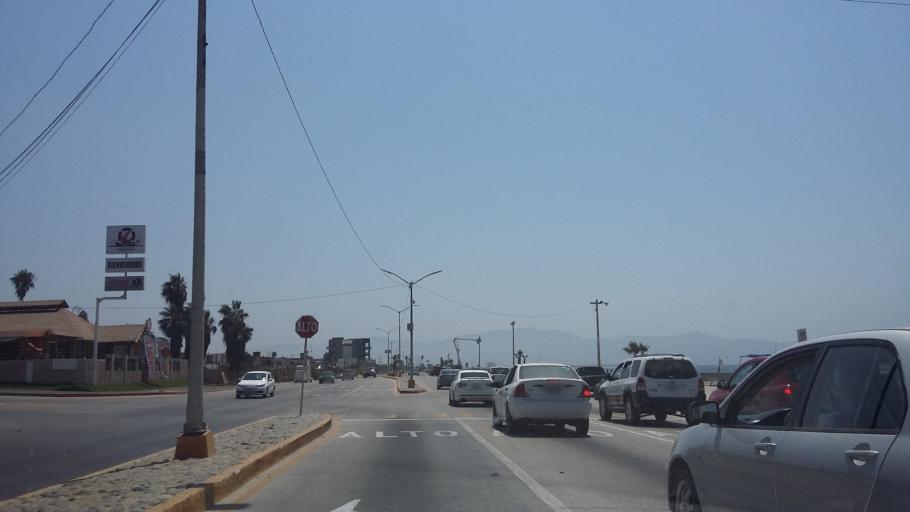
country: MX
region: Baja California
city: Ensenada
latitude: 31.8410
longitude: -116.6111
